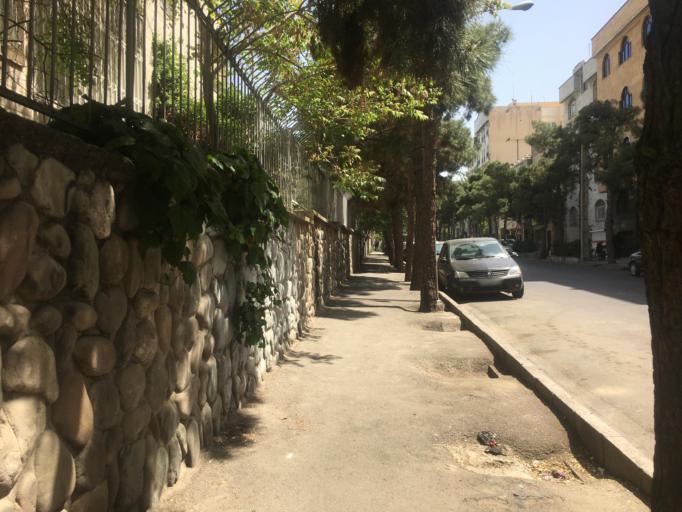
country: IR
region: Tehran
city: Tehran
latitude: 35.7433
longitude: 51.5472
